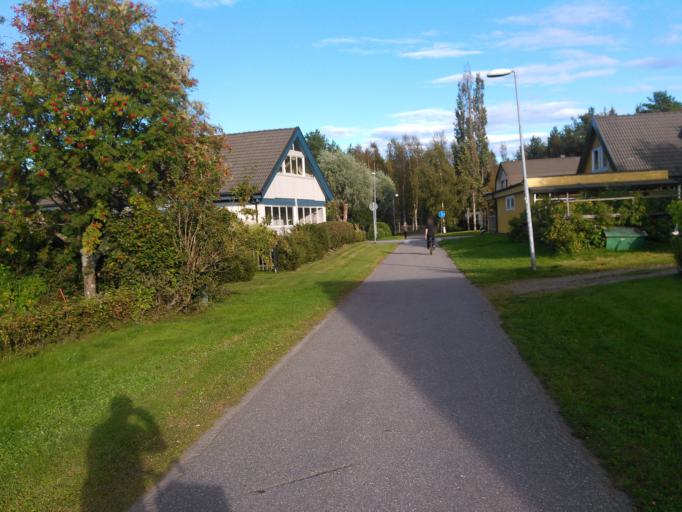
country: SE
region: Vaesterbotten
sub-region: Umea Kommun
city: Umea
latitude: 63.8094
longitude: 20.3297
